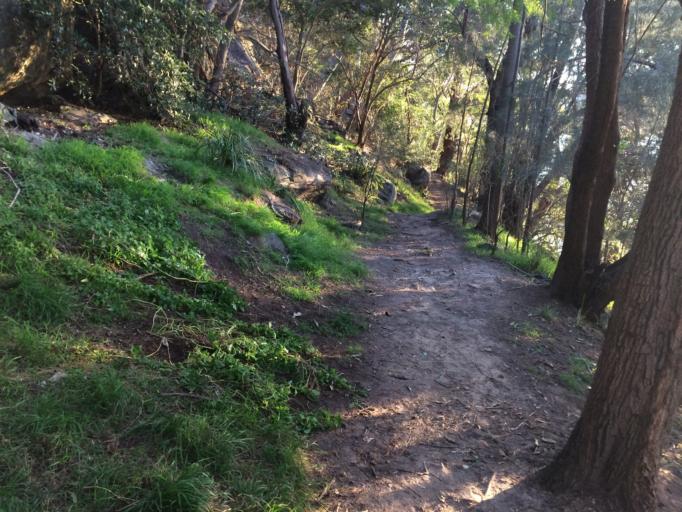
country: AU
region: New South Wales
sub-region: Lane Cove
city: Greenwich
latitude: -33.8377
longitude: 151.1831
